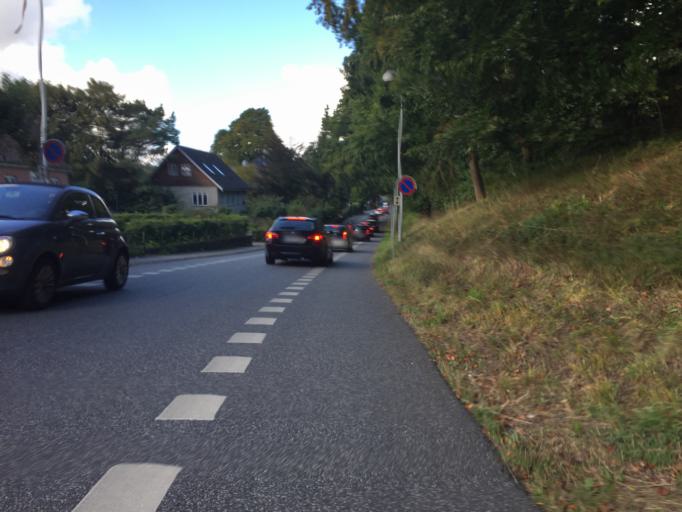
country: DK
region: Capital Region
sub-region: Fureso Kommune
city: Vaerlose
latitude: 55.7618
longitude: 12.4096
